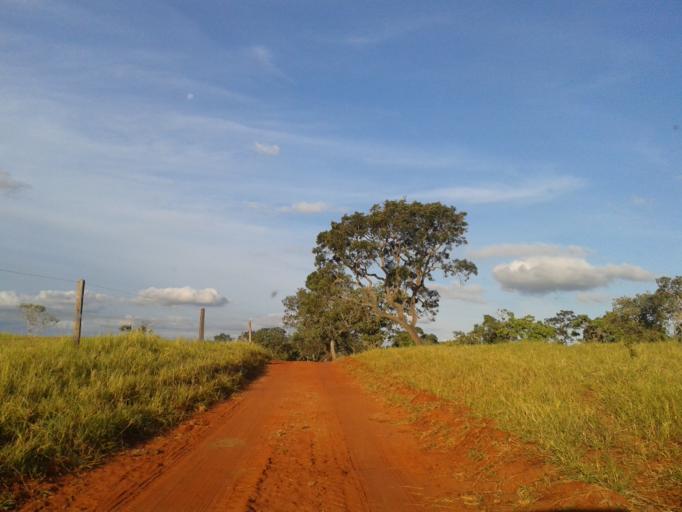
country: BR
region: Minas Gerais
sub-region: Campina Verde
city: Campina Verde
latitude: -19.4545
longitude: -49.6851
